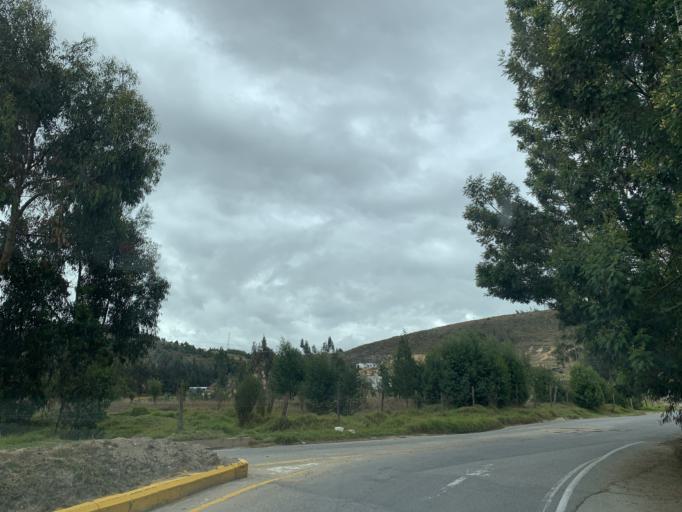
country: CO
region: Boyaca
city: Tunja
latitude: 5.5306
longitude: -73.3422
